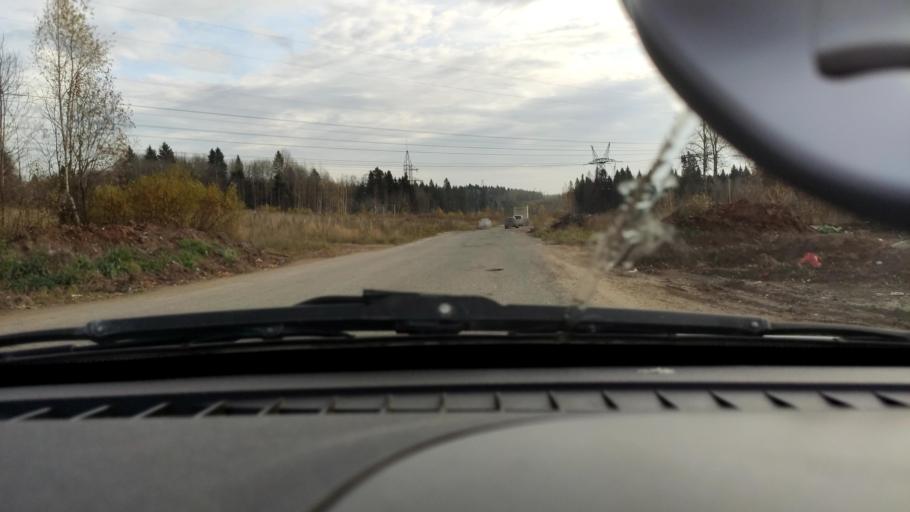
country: RU
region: Perm
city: Perm
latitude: 58.0888
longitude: 56.4184
